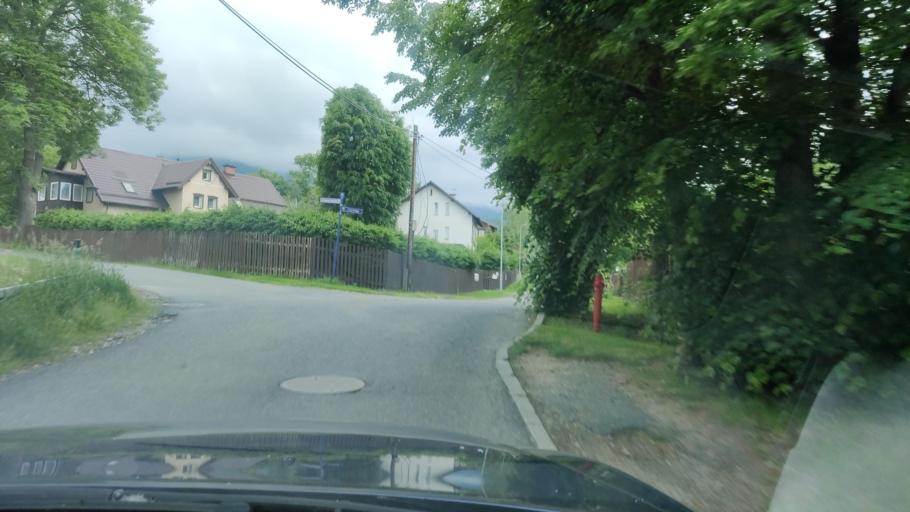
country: PL
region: Lower Silesian Voivodeship
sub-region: Powiat jeleniogorski
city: Karpacz
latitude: 50.7789
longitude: 15.7772
